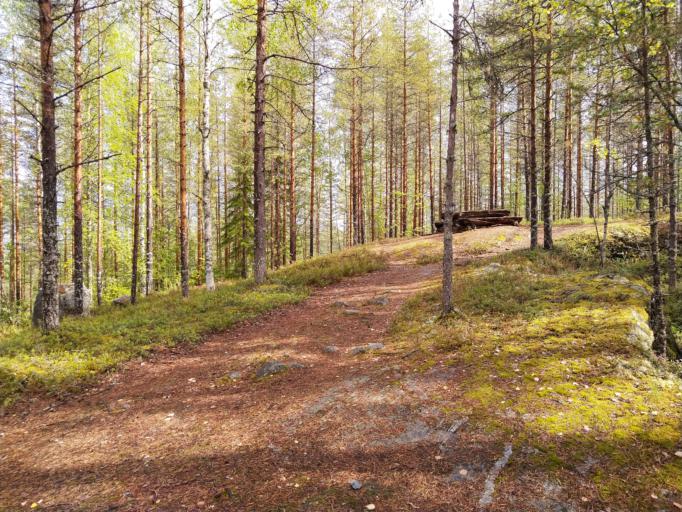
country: FI
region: North Karelia
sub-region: Pielisen Karjala
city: Lieksa
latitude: 63.5667
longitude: 30.1002
